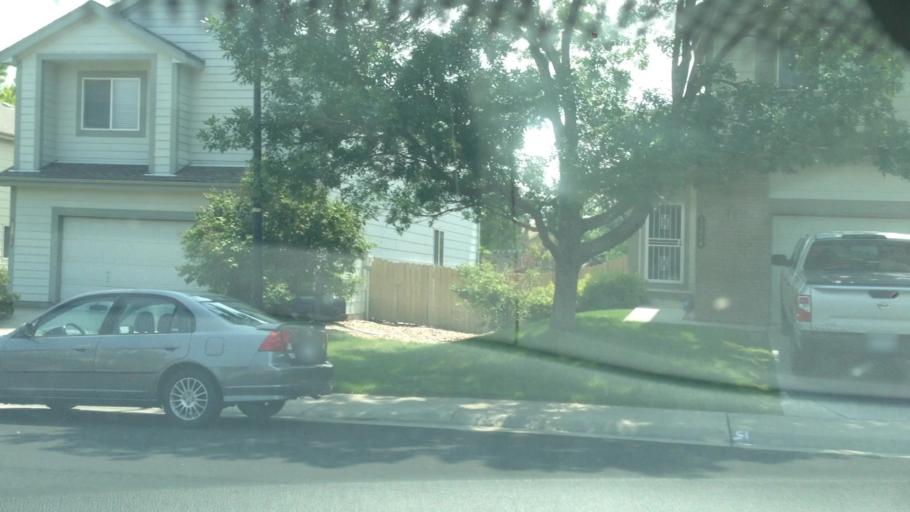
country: US
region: Colorado
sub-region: Douglas County
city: Stonegate
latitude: 39.5163
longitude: -104.7888
